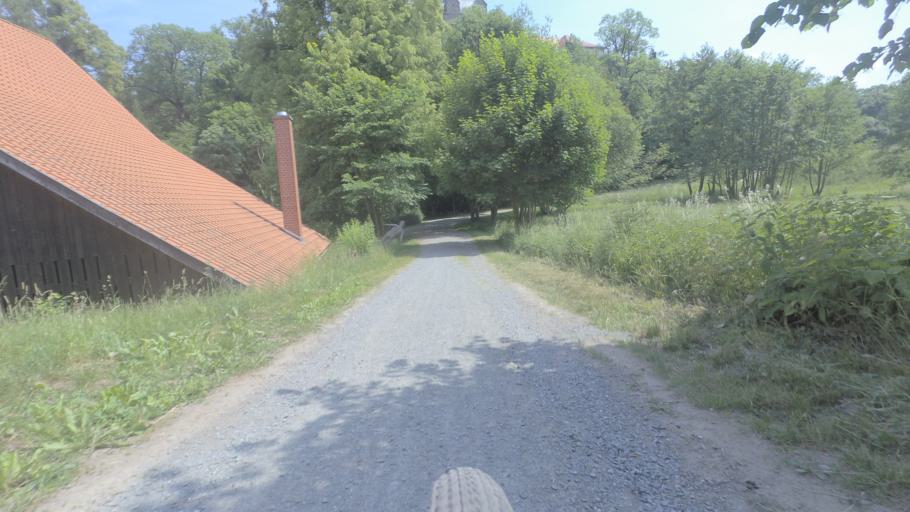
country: DE
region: Saxony-Anhalt
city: Ballenstedt
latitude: 51.7191
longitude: 11.2160
